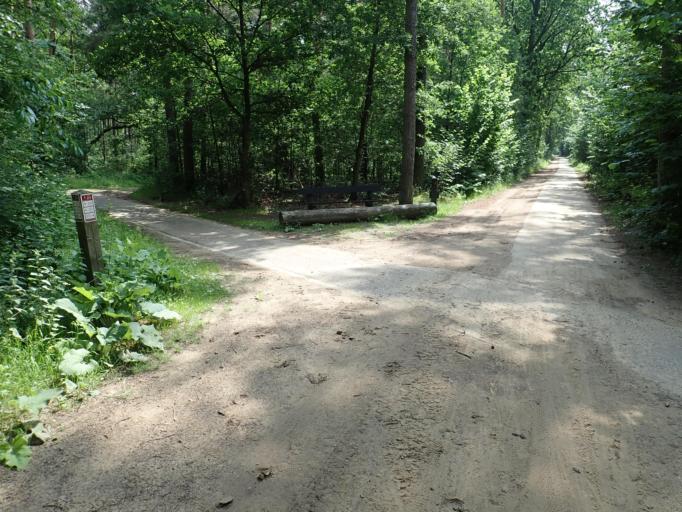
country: BE
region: Flanders
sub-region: Provincie Antwerpen
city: Kasterlee
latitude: 51.2173
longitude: 4.8965
